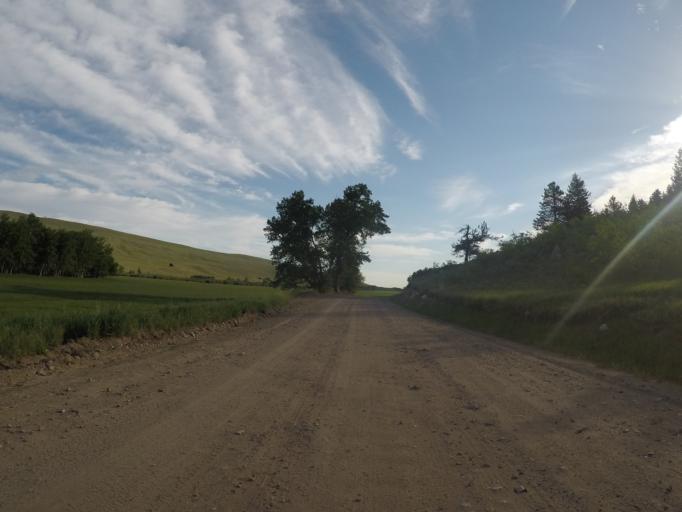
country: US
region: Montana
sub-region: Stillwater County
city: Absarokee
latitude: 45.2826
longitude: -109.5457
